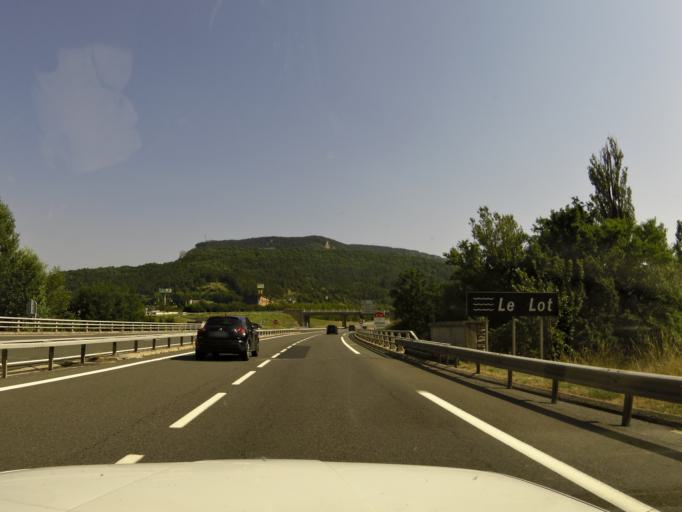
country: FR
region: Languedoc-Roussillon
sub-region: Departement de la Lozere
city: La Canourgue
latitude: 44.4394
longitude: 3.1948
